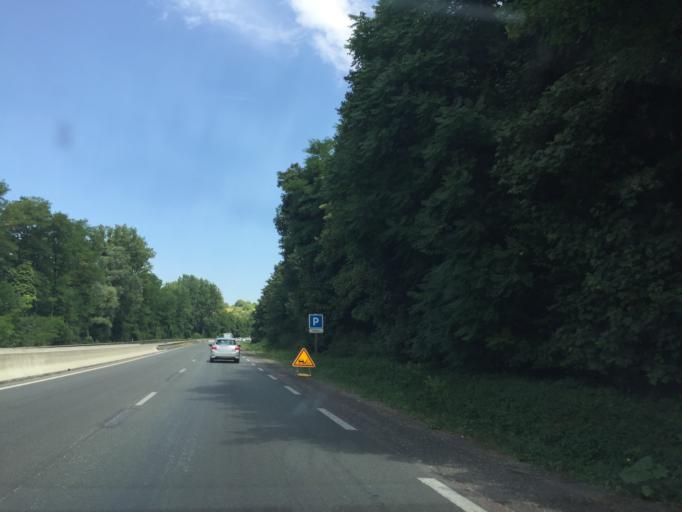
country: FR
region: Poitou-Charentes
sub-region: Departement de la Vienne
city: Biard
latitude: 46.5685
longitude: 0.3089
